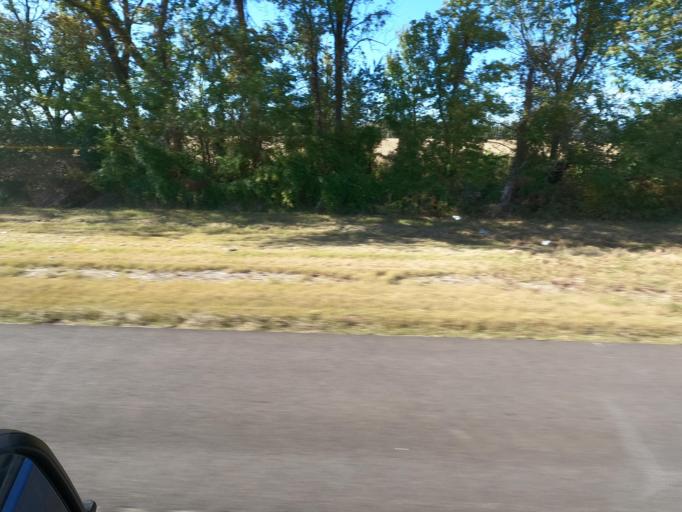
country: US
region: Tennessee
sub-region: Obion County
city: Obion
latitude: 36.2780
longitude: -89.2092
